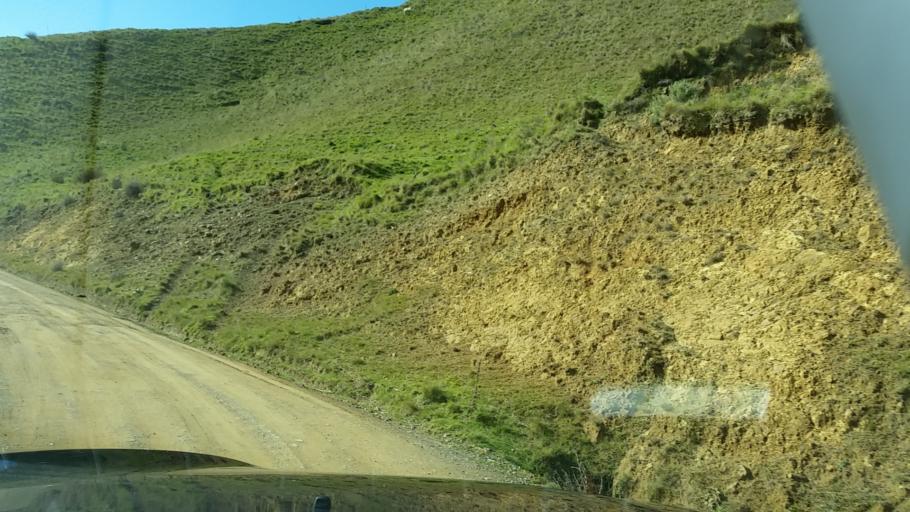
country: NZ
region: Marlborough
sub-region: Marlborough District
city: Picton
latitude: -40.9864
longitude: 173.8366
